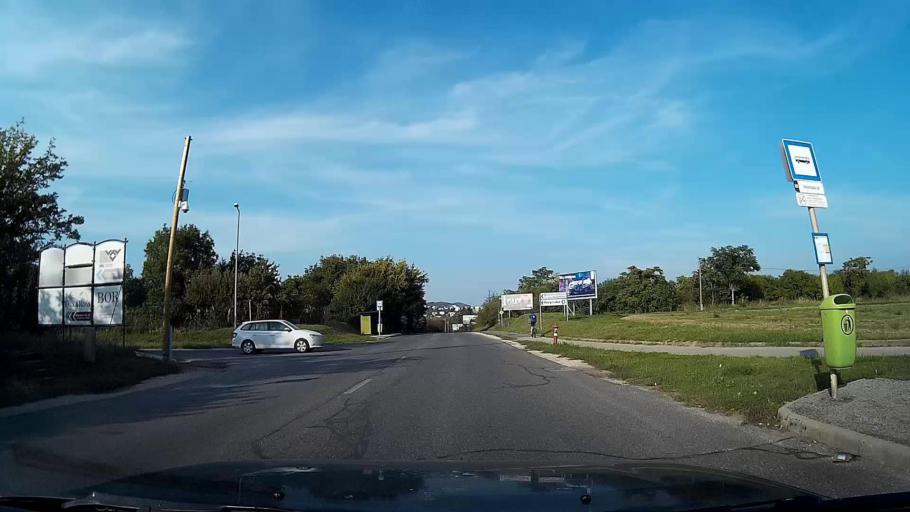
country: HU
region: Pest
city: Budaors
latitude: 47.4526
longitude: 18.9908
